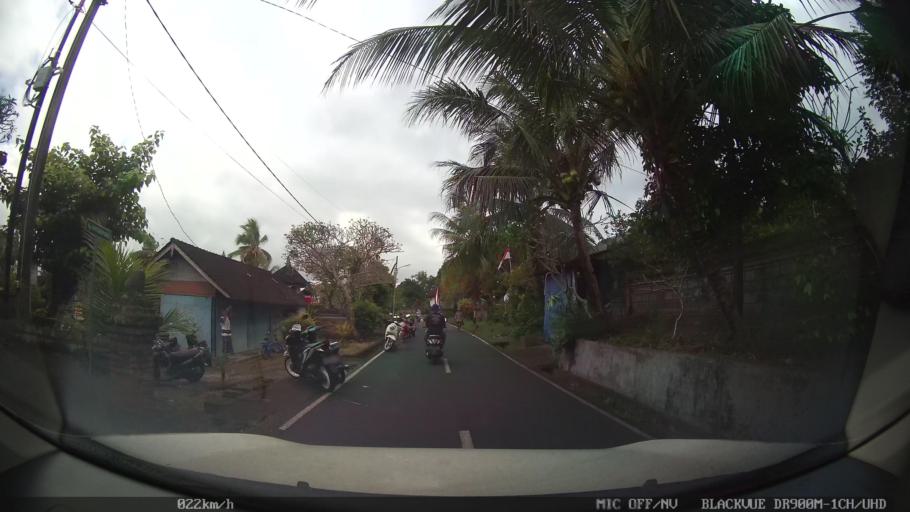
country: ID
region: Bali
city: Banjar Mambalkajanan
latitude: -8.5533
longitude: 115.2105
